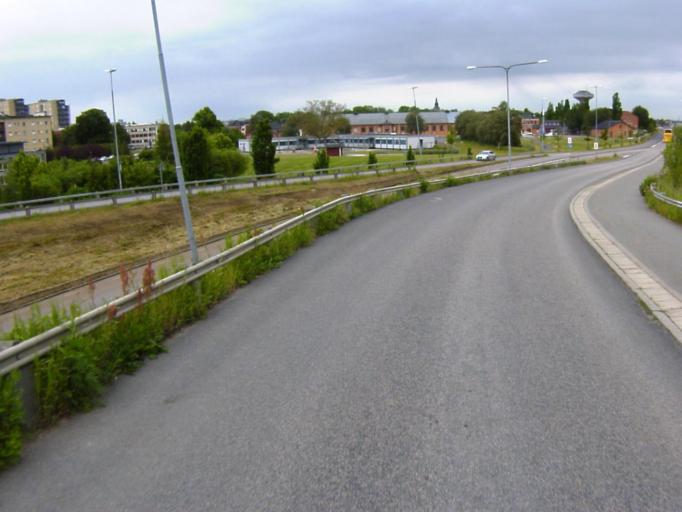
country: SE
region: Skane
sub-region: Kristianstads Kommun
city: Kristianstad
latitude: 56.0412
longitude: 14.1581
